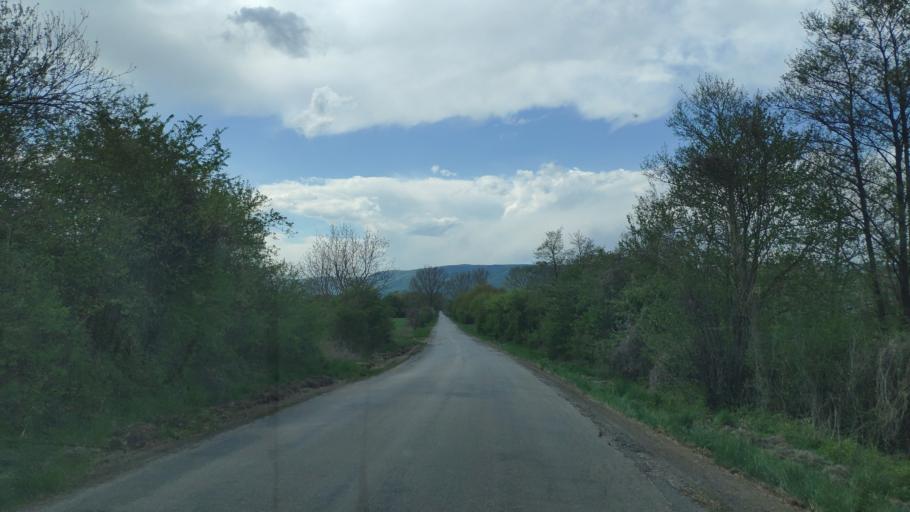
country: SK
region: Kosicky
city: Moldava nad Bodvou
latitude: 48.5901
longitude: 20.9076
